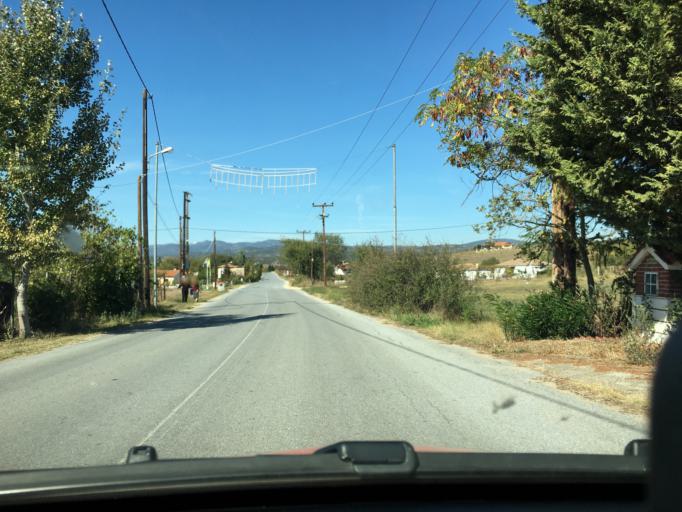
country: GR
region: Central Macedonia
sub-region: Nomos Chalkidikis
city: Megali Panagia
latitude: 40.3661
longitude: 23.6989
